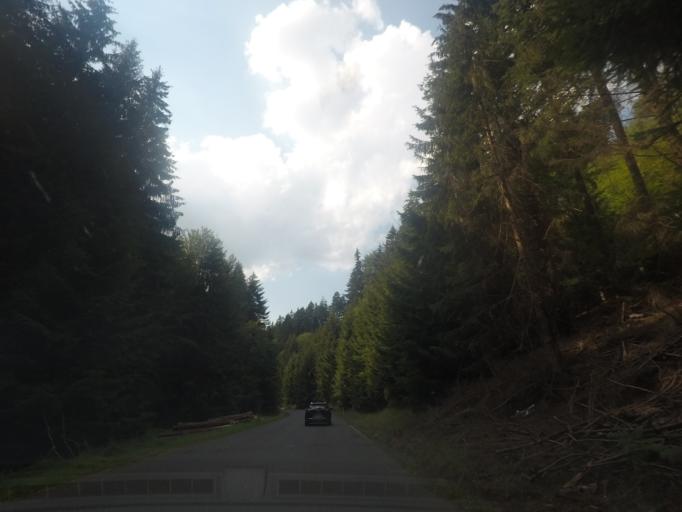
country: DE
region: Saxony
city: Sebnitz
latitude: 50.8782
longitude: 14.2798
